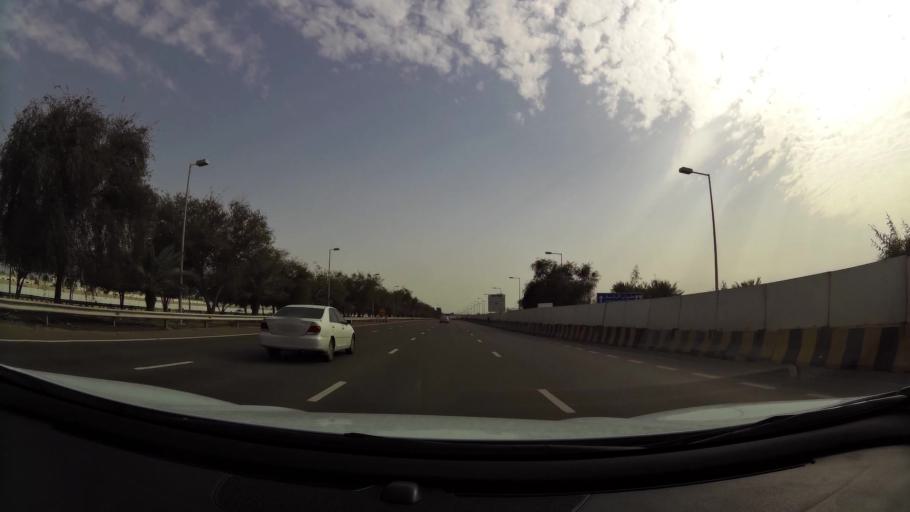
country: AE
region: Abu Dhabi
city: Abu Dhabi
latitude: 24.4394
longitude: 54.6781
